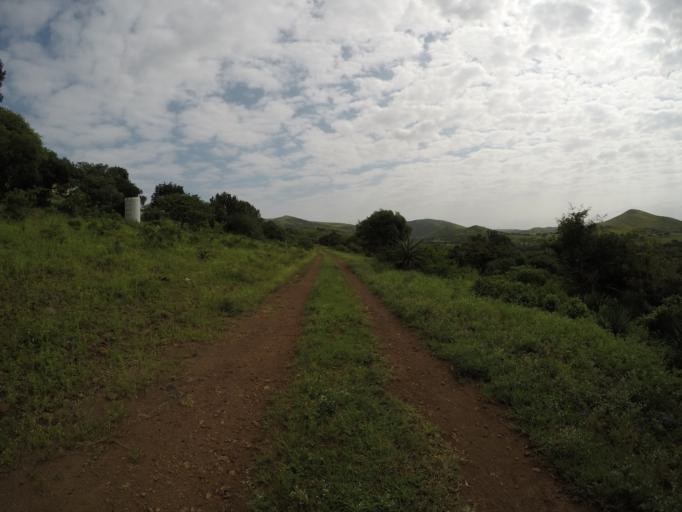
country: ZA
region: KwaZulu-Natal
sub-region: uThungulu District Municipality
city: Empangeni
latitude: -28.6285
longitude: 31.9099
